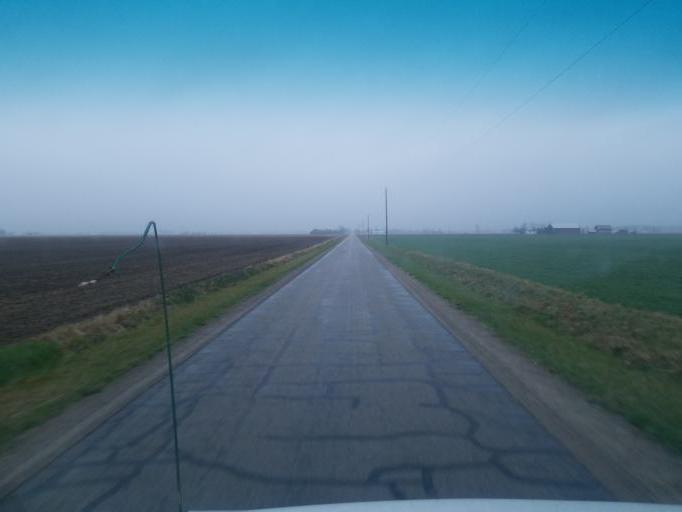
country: US
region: Ohio
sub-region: Henry County
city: Napoleon
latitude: 41.4133
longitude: -84.2273
